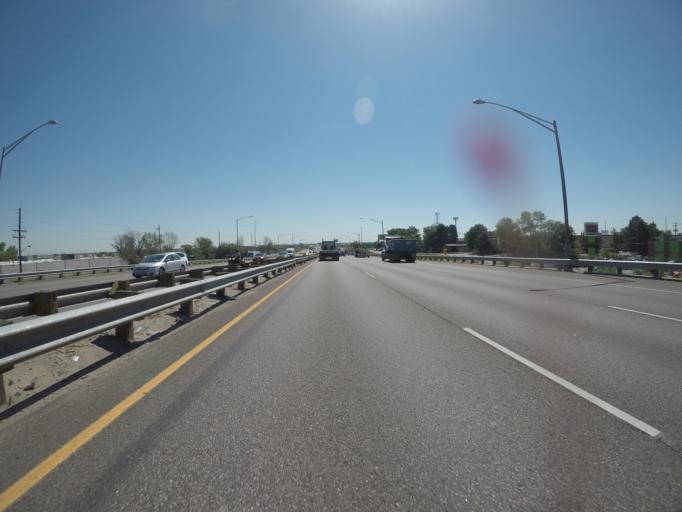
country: US
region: Colorado
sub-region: Adams County
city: Commerce City
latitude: 39.7784
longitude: -104.9116
